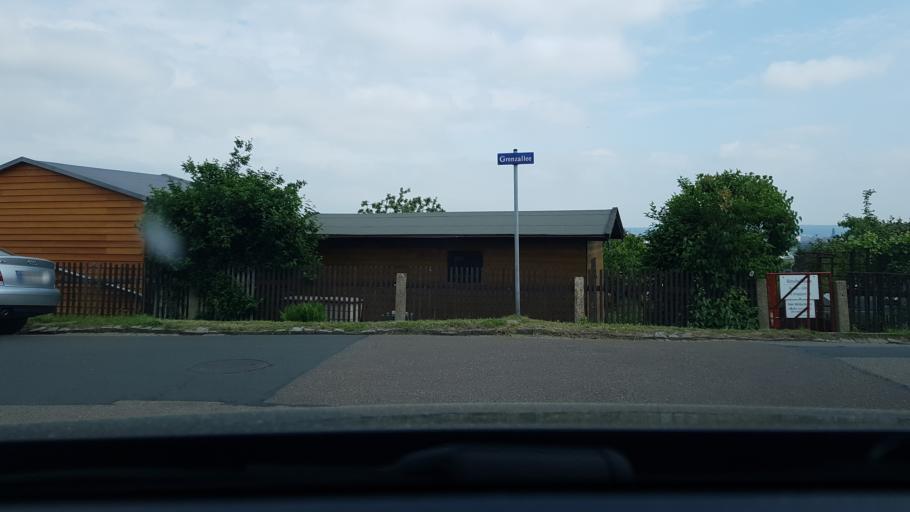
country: DE
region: Saxony
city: Bannewitz
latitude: 51.0304
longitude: 13.6958
